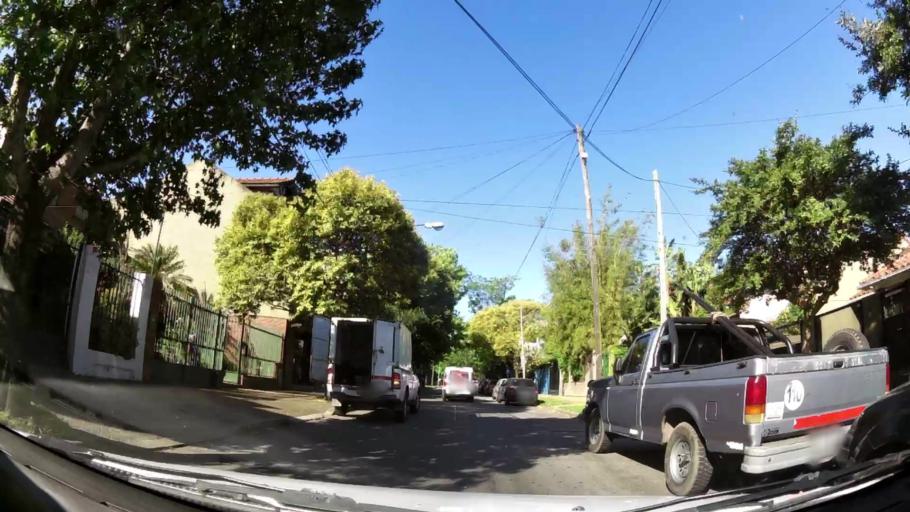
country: AR
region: Buenos Aires
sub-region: Partido de San Isidro
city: San Isidro
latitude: -34.4753
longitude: -58.5258
